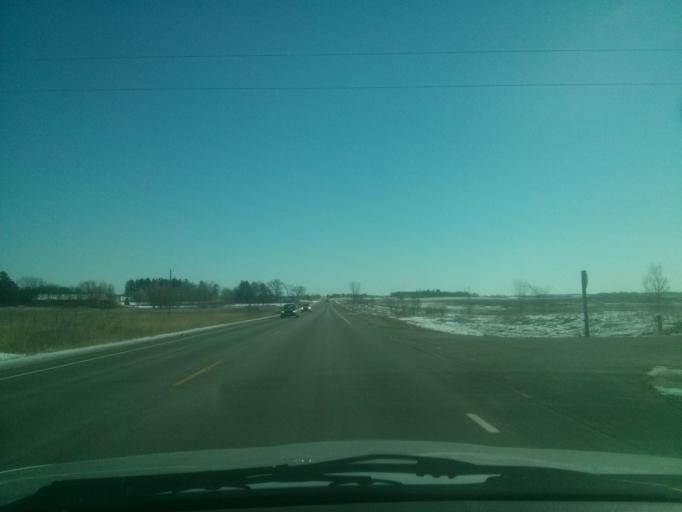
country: US
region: Wisconsin
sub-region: Polk County
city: Clear Lake
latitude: 45.1365
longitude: -92.3740
